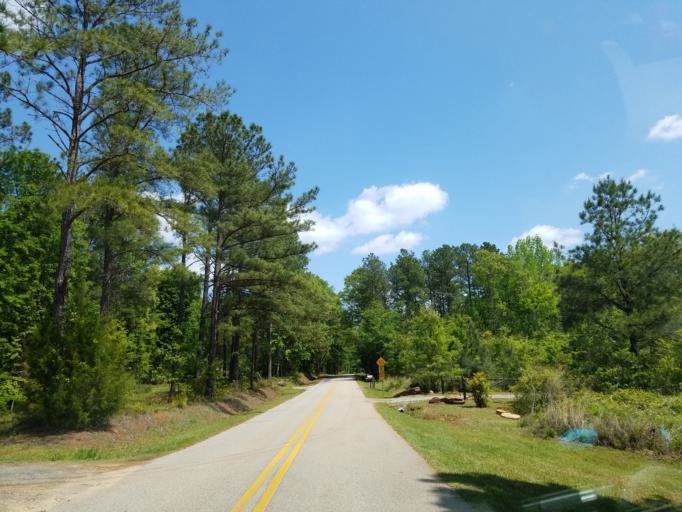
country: US
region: Georgia
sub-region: Monroe County
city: Forsyth
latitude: 33.1392
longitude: -83.9826
